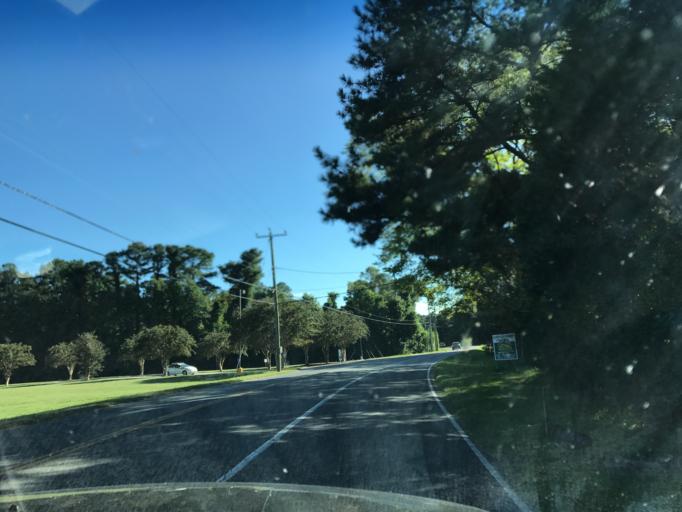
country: US
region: Virginia
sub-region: City of Portsmouth
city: Portsmouth Heights
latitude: 36.7397
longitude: -76.3444
